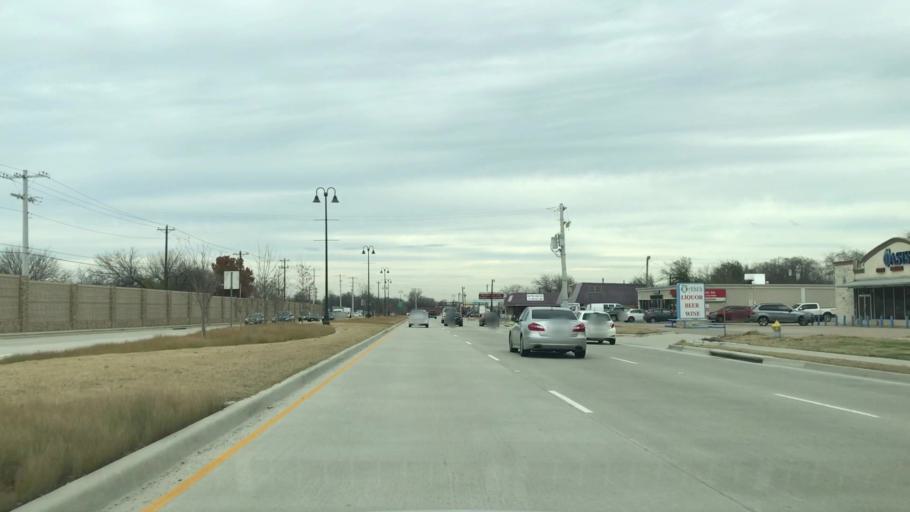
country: US
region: Texas
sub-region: Denton County
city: The Colony
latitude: 33.0997
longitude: -96.8925
